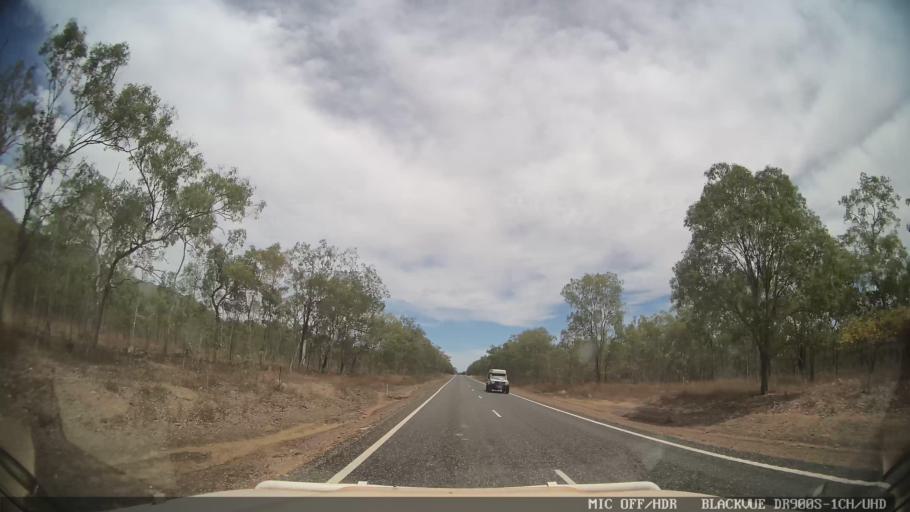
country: AU
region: Queensland
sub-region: Cairns
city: Port Douglas
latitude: -16.2443
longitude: 144.7269
